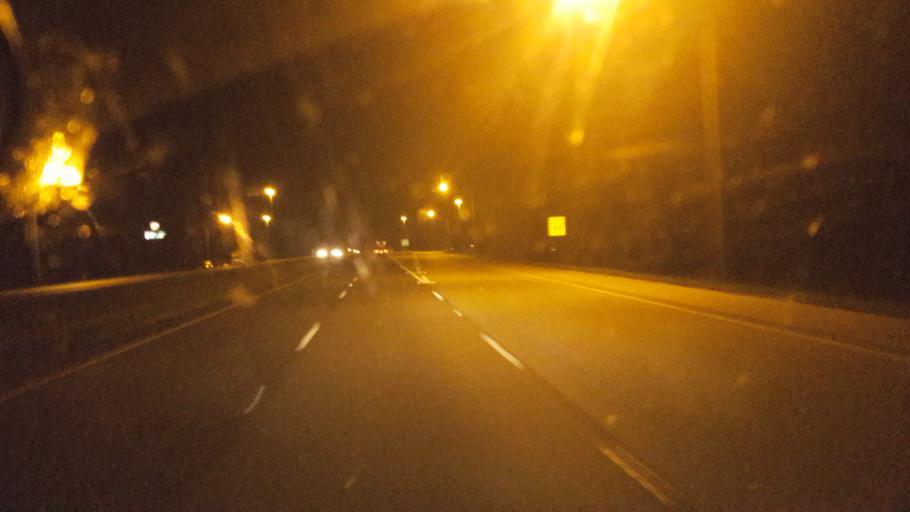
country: US
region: Indiana
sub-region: Clay County
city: Brazil
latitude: 39.4493
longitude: -87.1204
